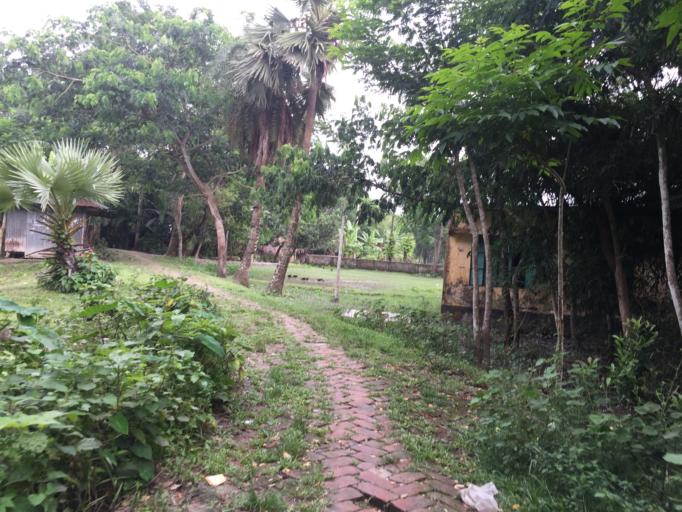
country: BD
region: Barisal
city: Mathba
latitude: 22.1894
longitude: 89.9248
